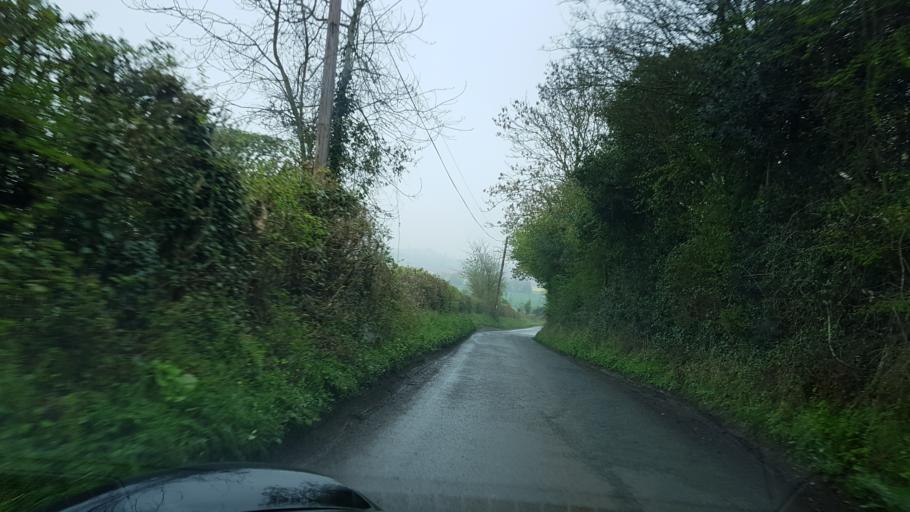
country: GB
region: England
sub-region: Herefordshire
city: Yatton
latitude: 52.0084
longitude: -2.5218
